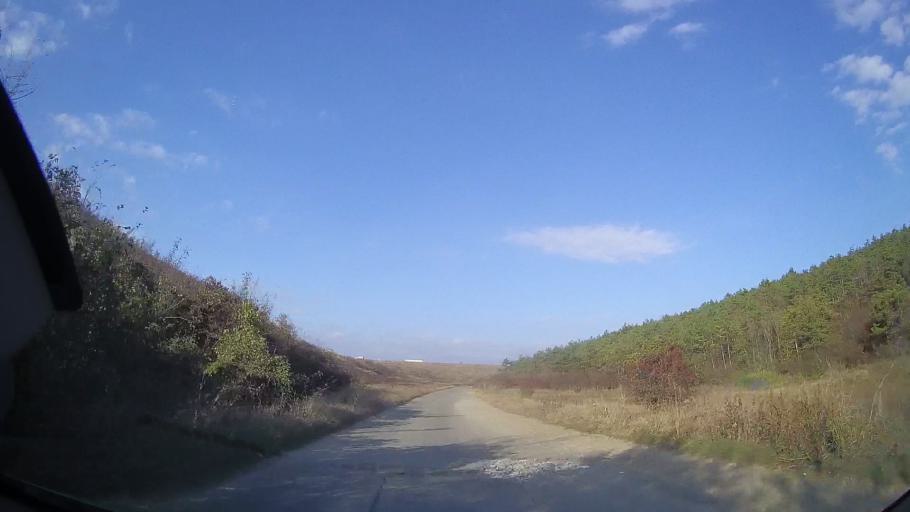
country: RO
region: Constanta
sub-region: Comuna Limanu
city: Limanu
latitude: 43.8160
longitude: 28.5175
